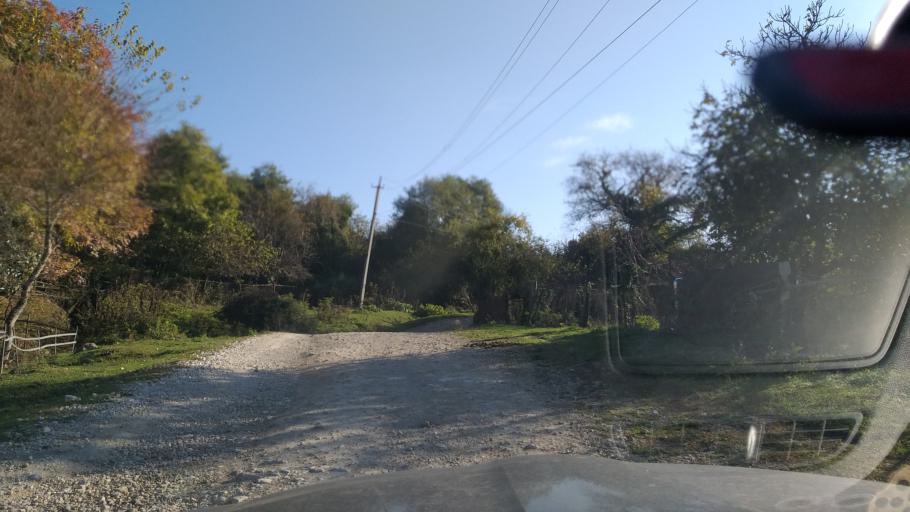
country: GE
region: Abkhazia
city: Stantsiya Novyy Afon
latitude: 43.0629
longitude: 40.8895
